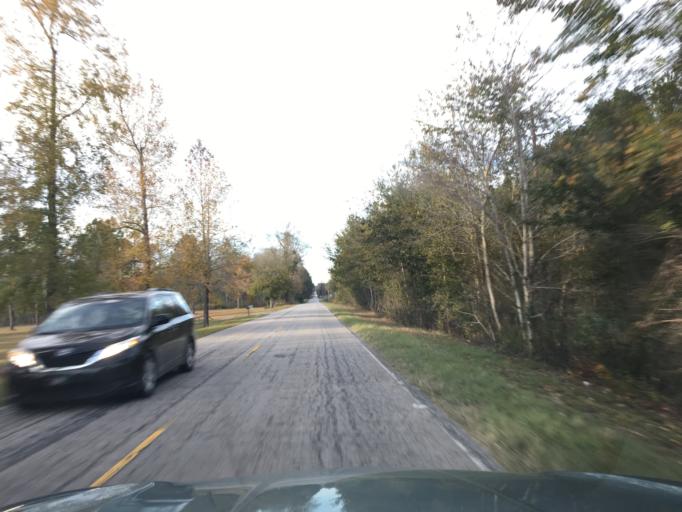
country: US
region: South Carolina
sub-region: Lexington County
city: Red Bank
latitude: 33.7251
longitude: -81.3580
